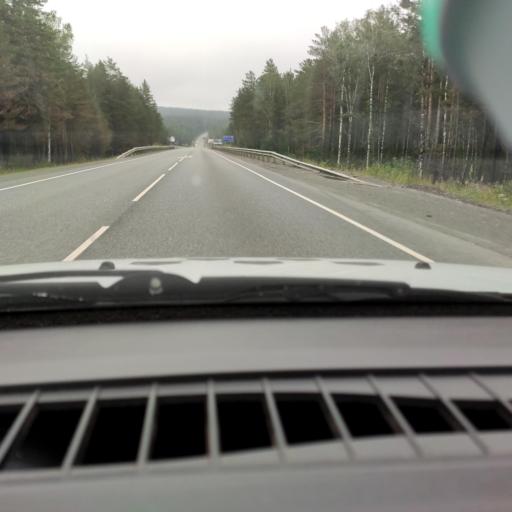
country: RU
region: Chelyabinsk
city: Zlatoust
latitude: 55.0559
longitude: 59.6894
